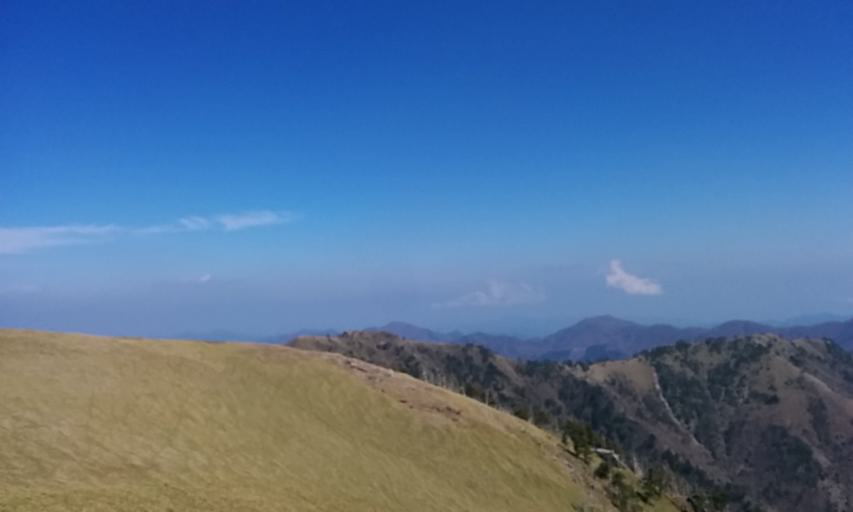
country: JP
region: Tokushima
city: Wakimachi
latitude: 33.8544
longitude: 134.0950
